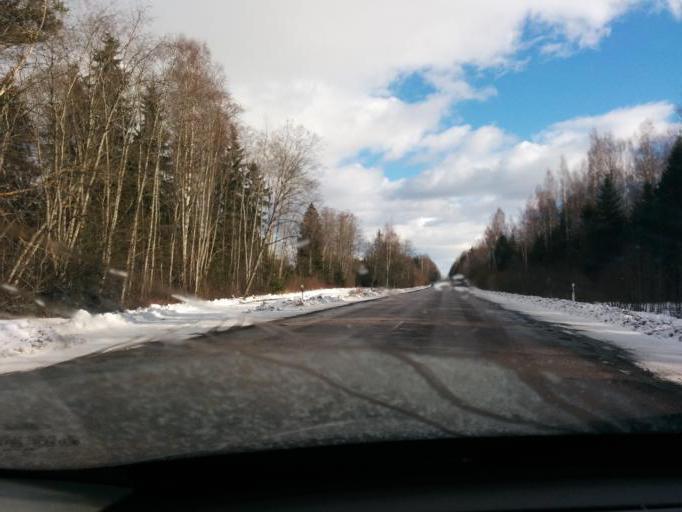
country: LV
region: Cesvaine
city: Cesvaine
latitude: 57.2365
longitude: 26.4336
